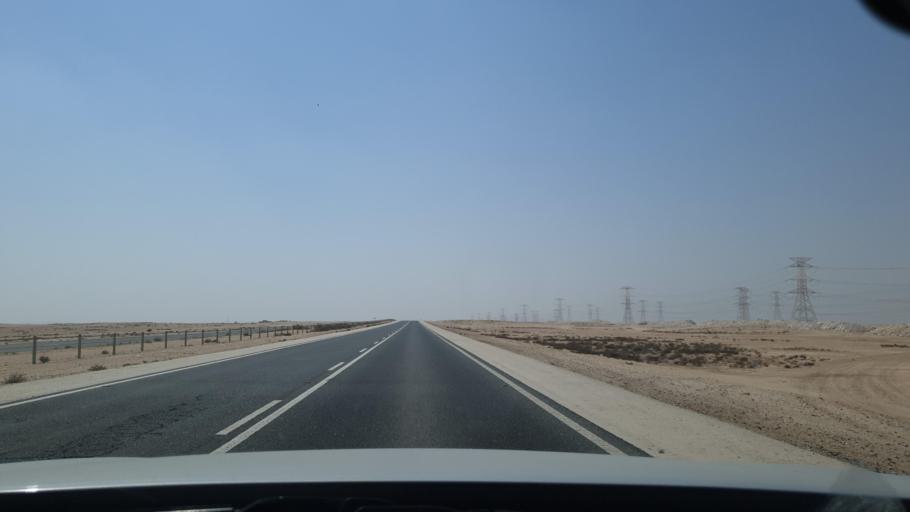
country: QA
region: Al Khawr
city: Al Khawr
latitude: 25.7247
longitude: 51.4539
